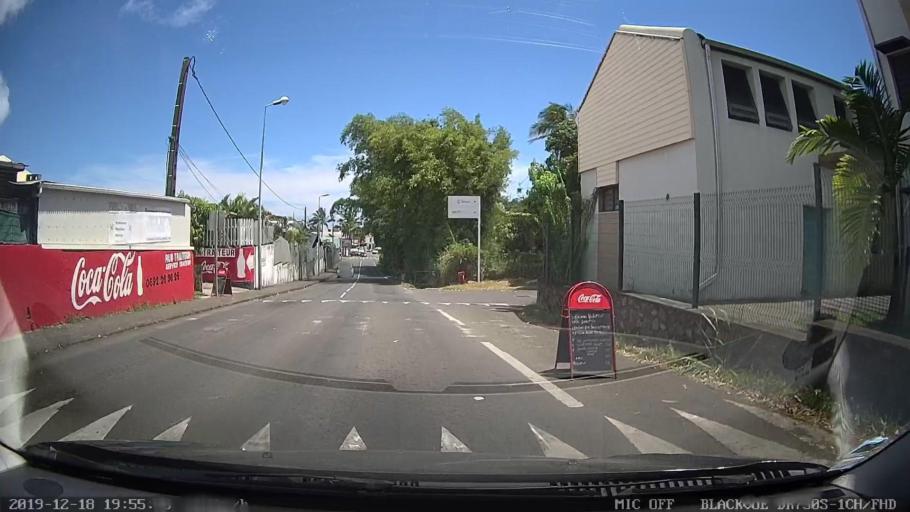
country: RE
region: Reunion
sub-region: Reunion
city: Saint-Andre
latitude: -20.9323
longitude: 55.6385
